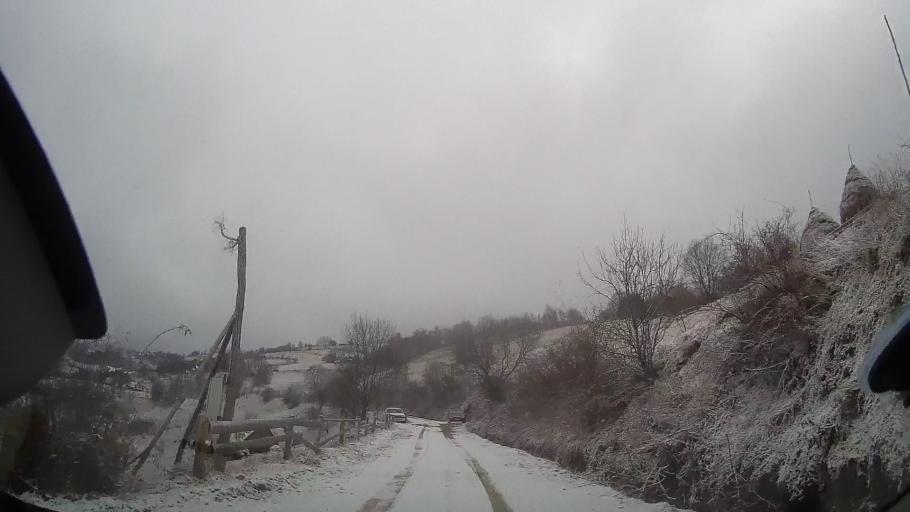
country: RO
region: Cluj
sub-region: Comuna Maguri-Racatau
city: Maguri-Racatau
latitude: 46.6613
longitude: 23.1913
